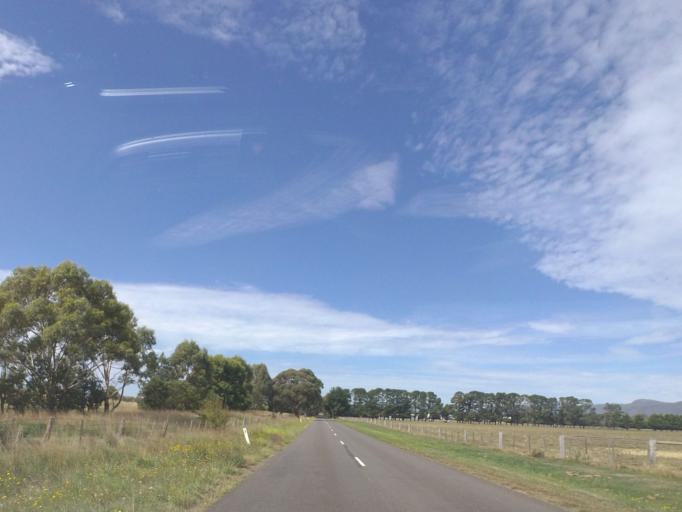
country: AU
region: Victoria
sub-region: Hume
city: Sunbury
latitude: -37.3220
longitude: 144.5311
